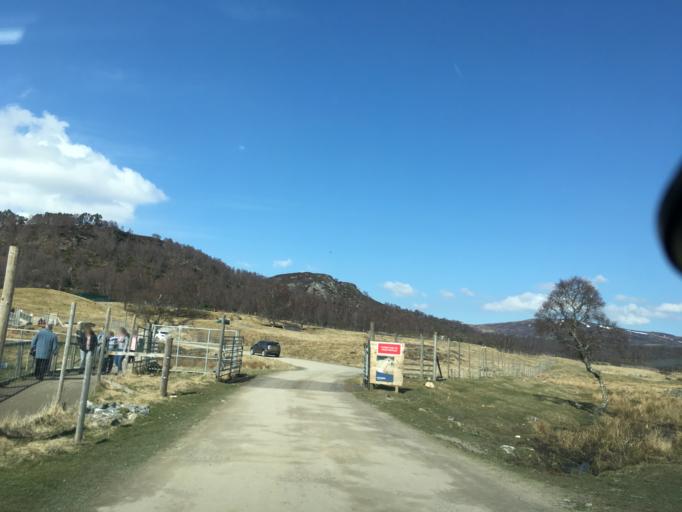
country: GB
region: Scotland
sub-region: Highland
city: Kingussie
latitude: 57.1087
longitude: -3.9804
